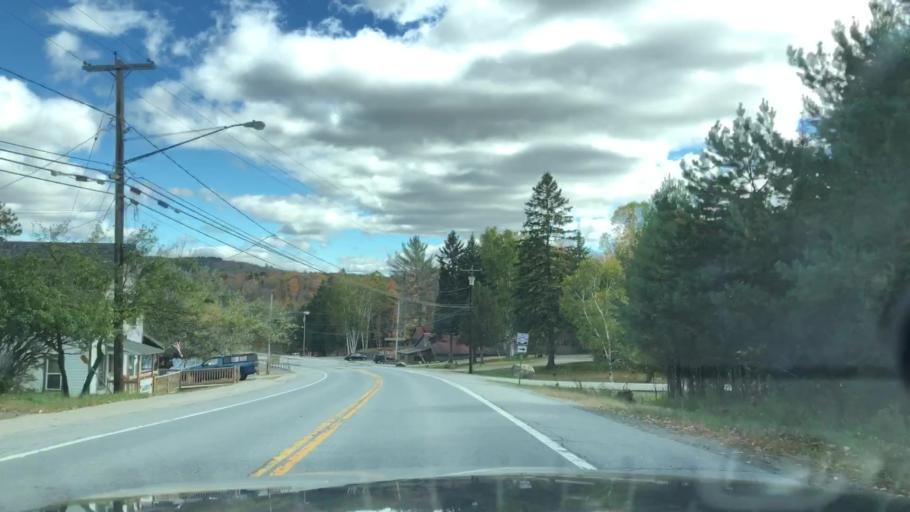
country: US
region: New York
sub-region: Hamilton County
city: Lake Pleasant
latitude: 43.7814
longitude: -74.2587
